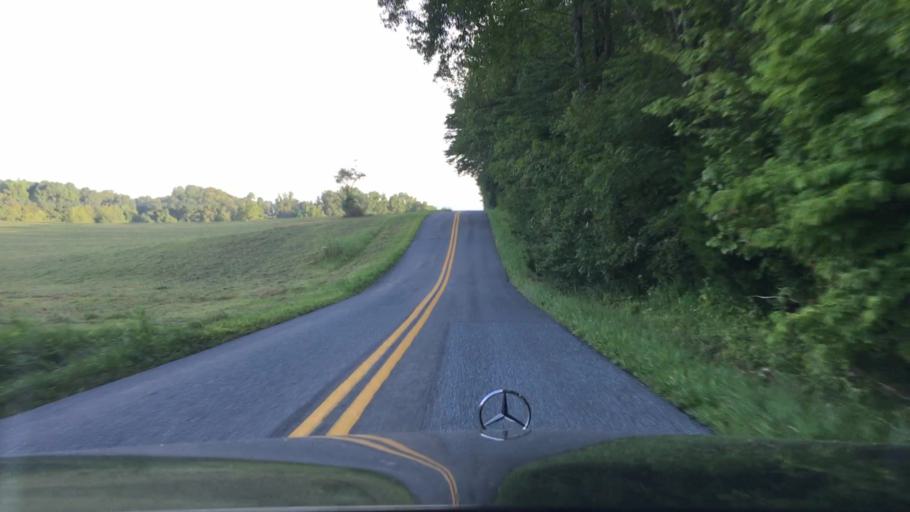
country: US
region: Virginia
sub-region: Campbell County
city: Timberlake
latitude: 37.2734
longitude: -79.2665
